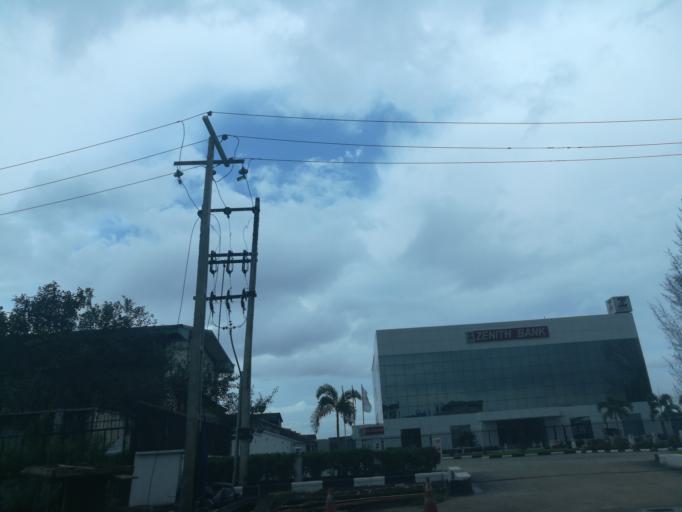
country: NG
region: Lagos
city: Agege
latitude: 6.6132
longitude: 3.3357
